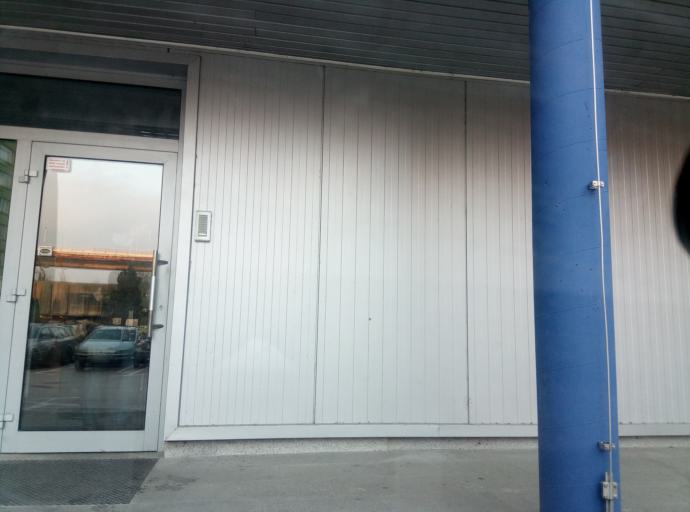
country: SI
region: Kranj
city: Kranj
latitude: 46.2266
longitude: 14.3619
